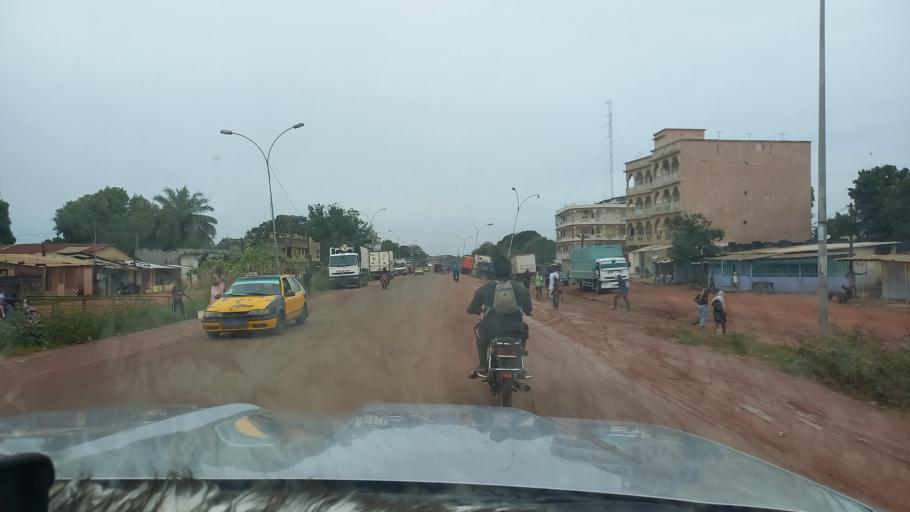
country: SN
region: Ziguinchor
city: Ziguinchor
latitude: 12.5664
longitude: -16.2684
